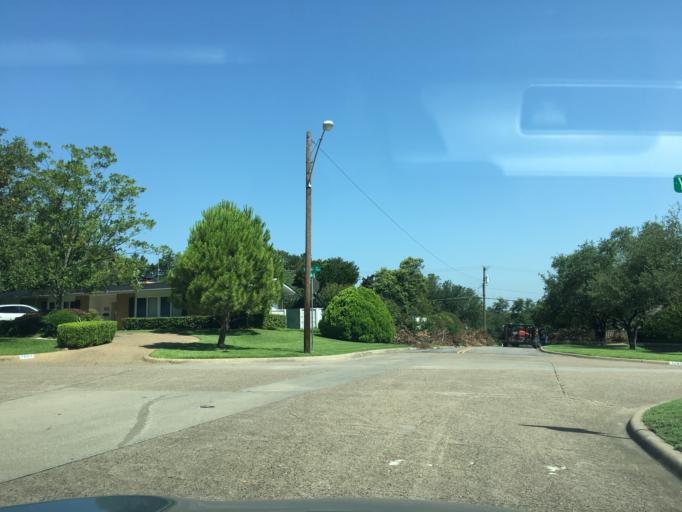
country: US
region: Texas
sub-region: Dallas County
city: University Park
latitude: 32.9034
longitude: -96.7758
